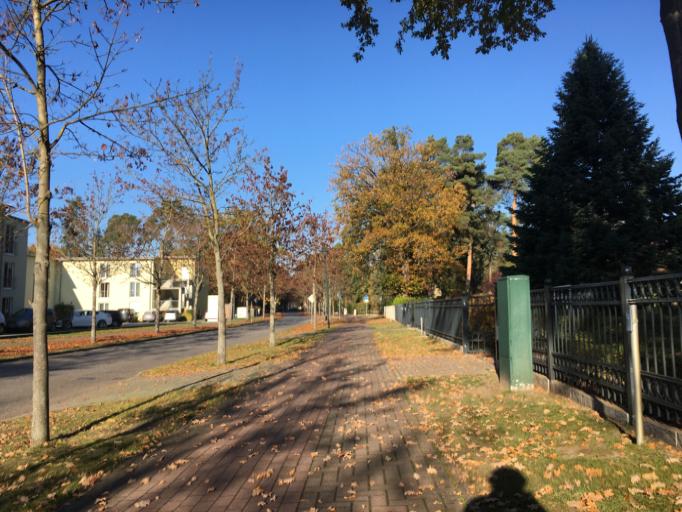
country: DE
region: Brandenburg
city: Bad Saarow
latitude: 52.2747
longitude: 14.0610
